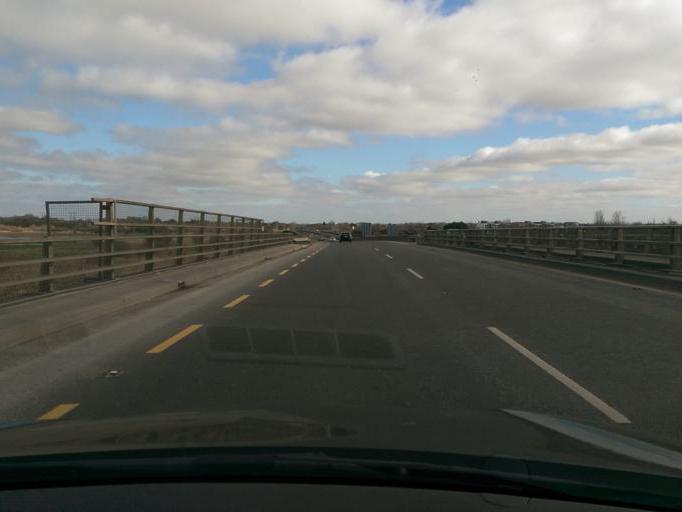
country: IE
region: Leinster
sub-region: An Iarmhi
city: Athlone
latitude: 53.4291
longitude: -7.9613
